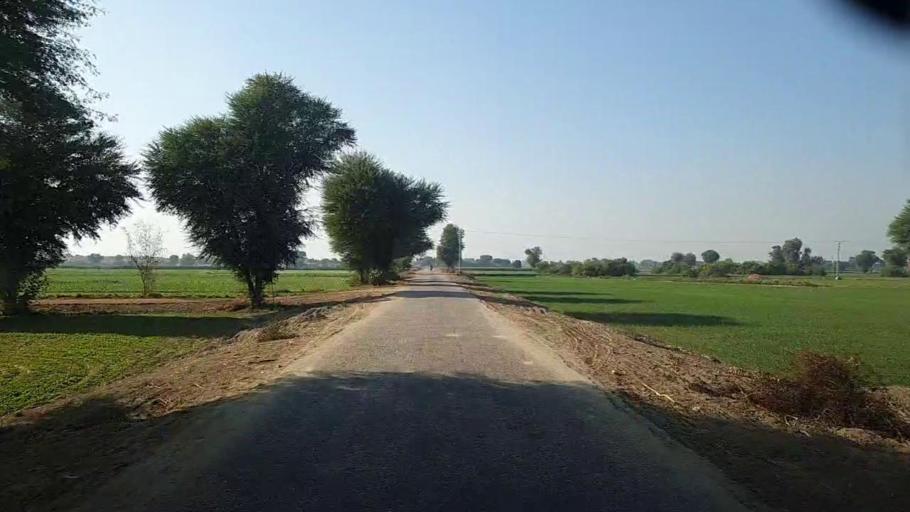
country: PK
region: Sindh
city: Darya Khan Marri
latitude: 26.6854
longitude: 68.3540
